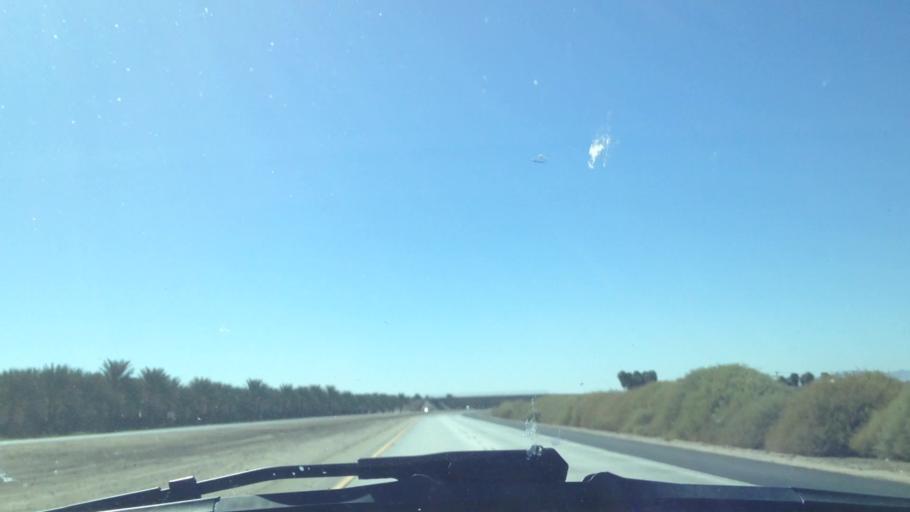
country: US
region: California
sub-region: Riverside County
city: Thermal
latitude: 33.6319
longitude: -116.1255
